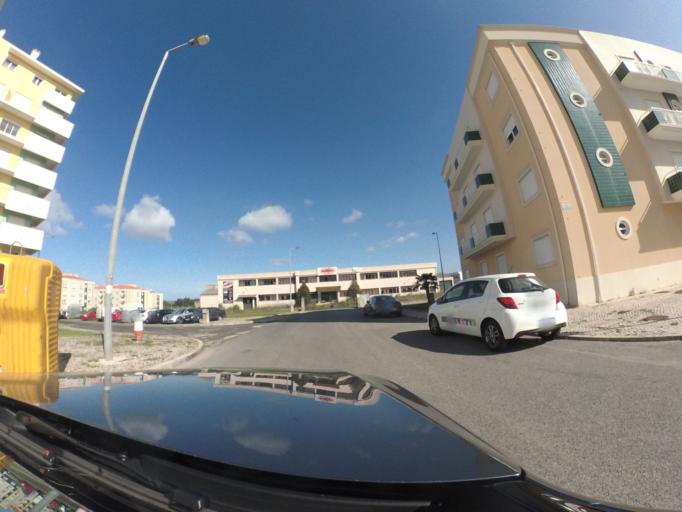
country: PT
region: Leiria
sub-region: Caldas da Rainha
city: Caldas da Rainha
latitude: 39.4138
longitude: -9.1367
